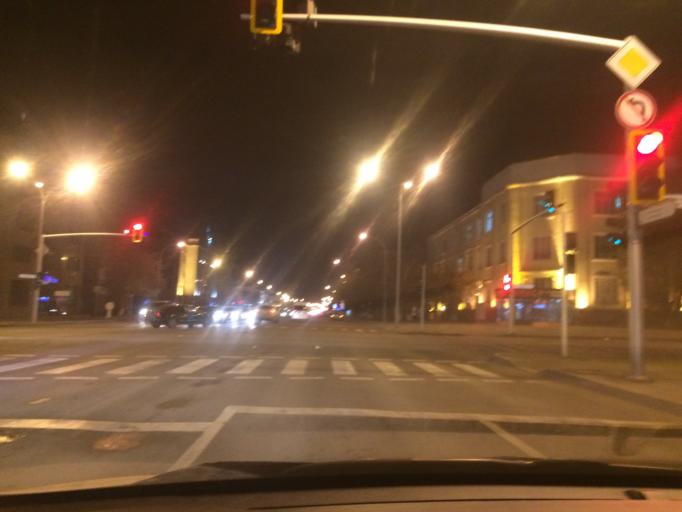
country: KZ
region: Astana Qalasy
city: Astana
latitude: 51.1653
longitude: 71.4142
